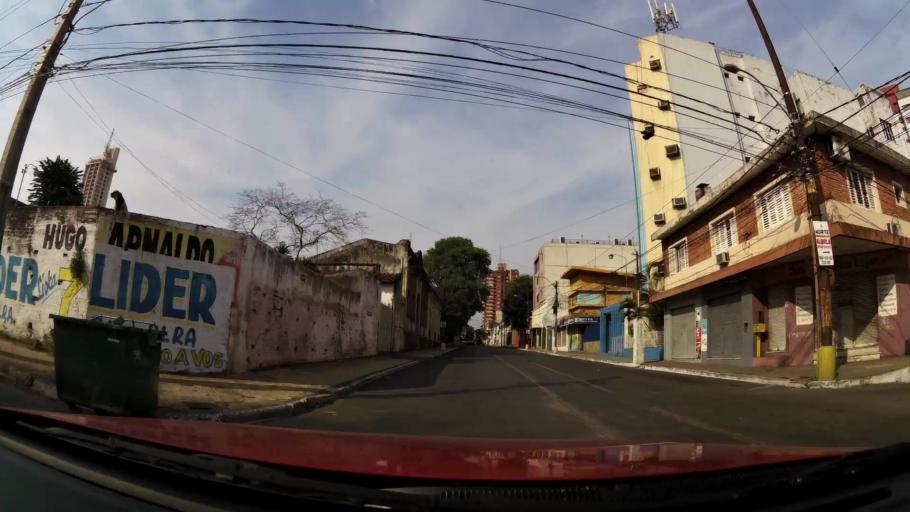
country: PY
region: Asuncion
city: Asuncion
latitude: -25.2850
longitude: -57.6247
